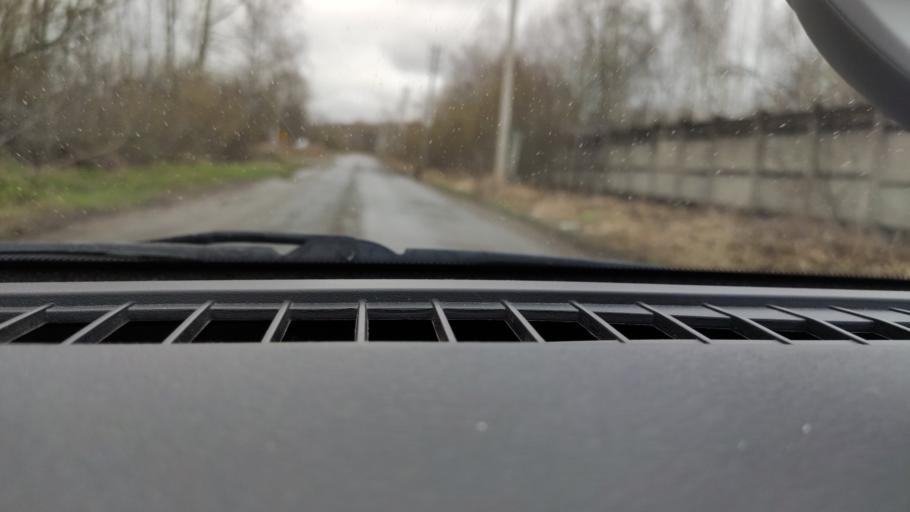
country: RU
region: Perm
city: Perm
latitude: 58.1056
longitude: 56.3553
